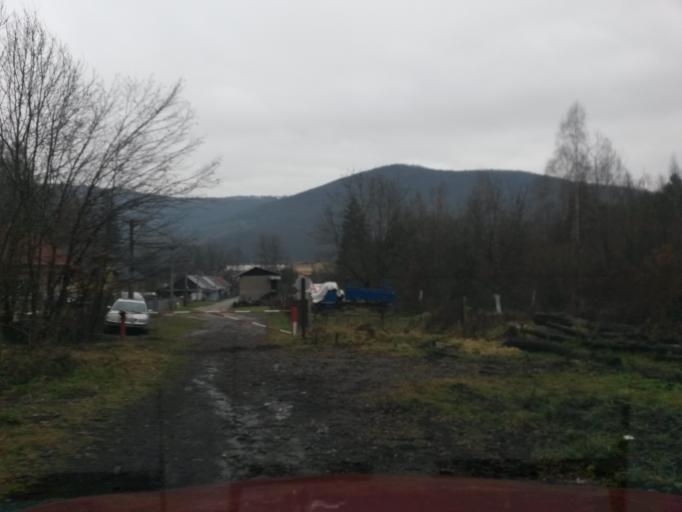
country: SK
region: Kosicky
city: Dobsina
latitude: 48.7436
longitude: 20.4107
